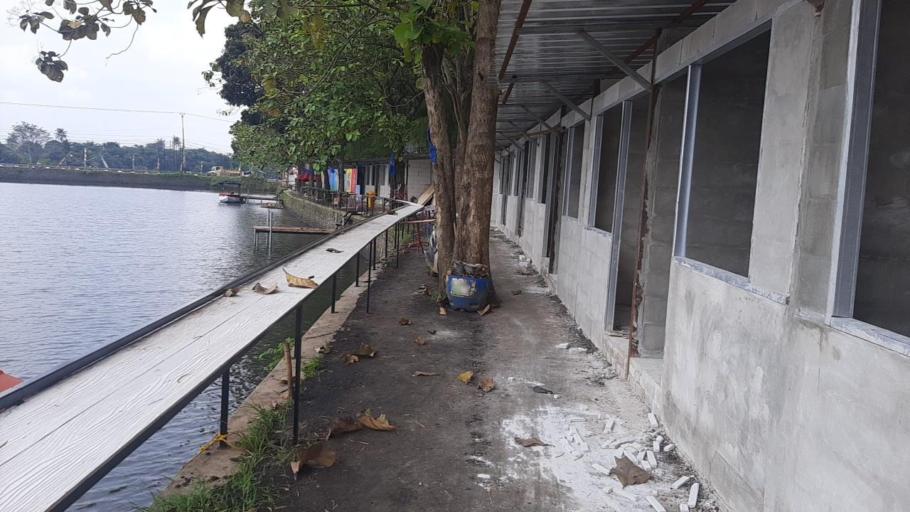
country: ID
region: West Java
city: Cileungsir
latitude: -6.4199
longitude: 107.0298
